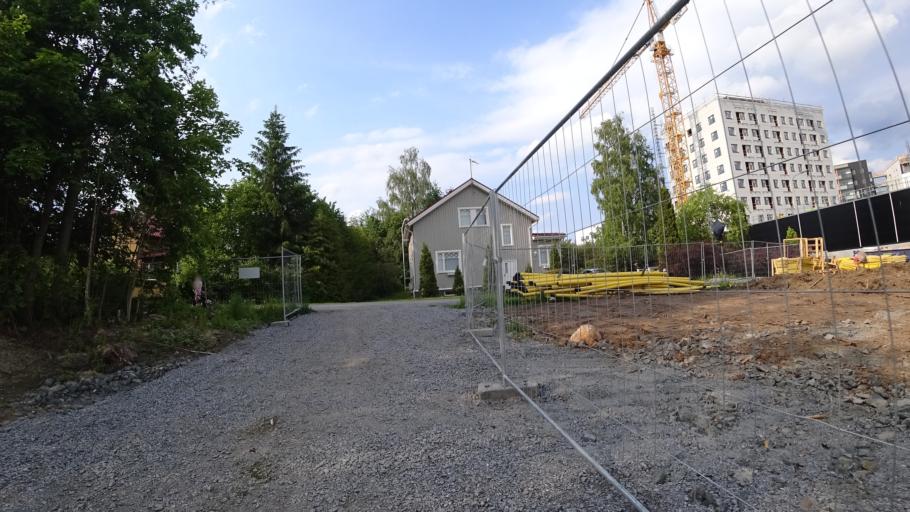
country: FI
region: Pirkanmaa
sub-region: Tampere
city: Pirkkala
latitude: 61.5036
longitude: 23.6288
